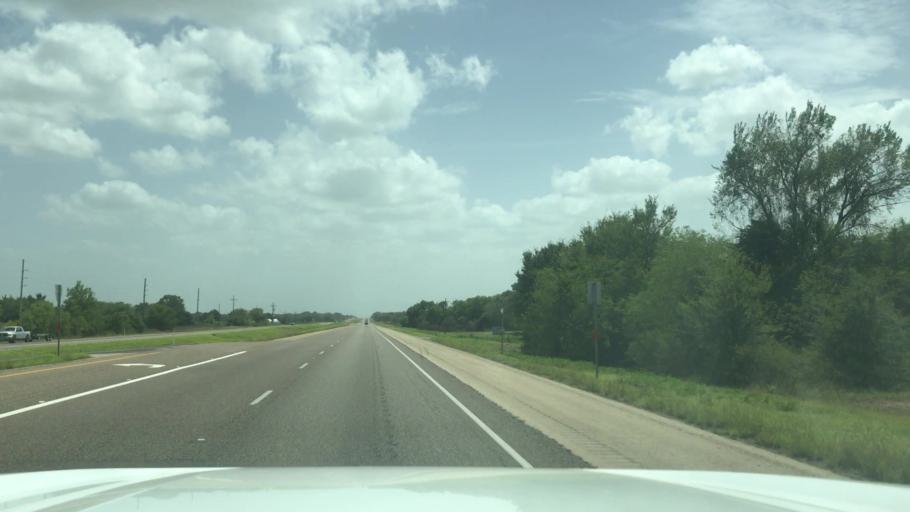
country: US
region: Texas
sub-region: Robertson County
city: Calvert
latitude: 31.0808
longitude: -96.7137
